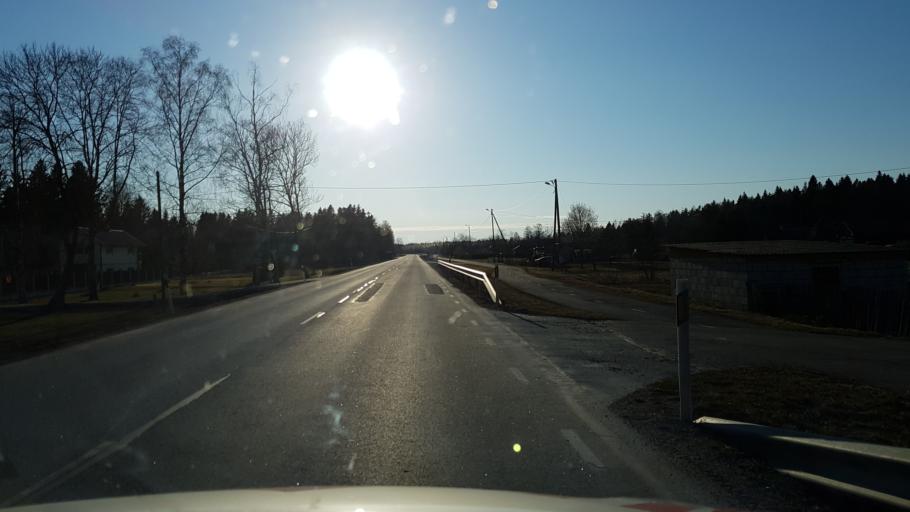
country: EE
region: Ida-Virumaa
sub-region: Kivioli linn
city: Kivioli
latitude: 59.3554
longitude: 26.9152
